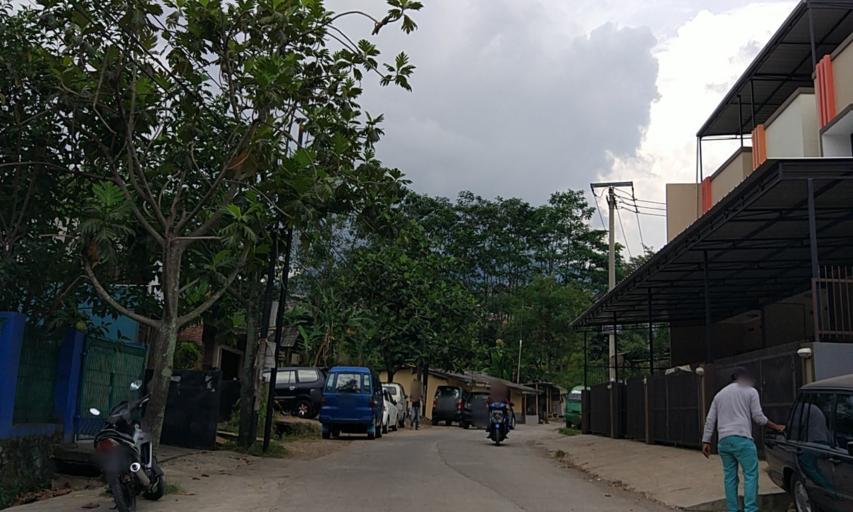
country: ID
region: West Java
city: Cileunyi
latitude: -6.9006
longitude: 107.6929
